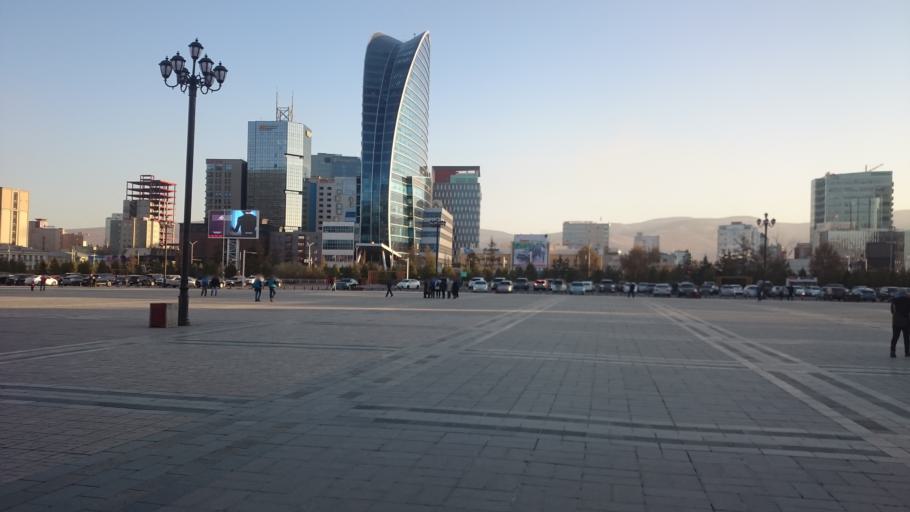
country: MN
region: Ulaanbaatar
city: Ulaanbaatar
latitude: 47.9187
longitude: 106.9170
